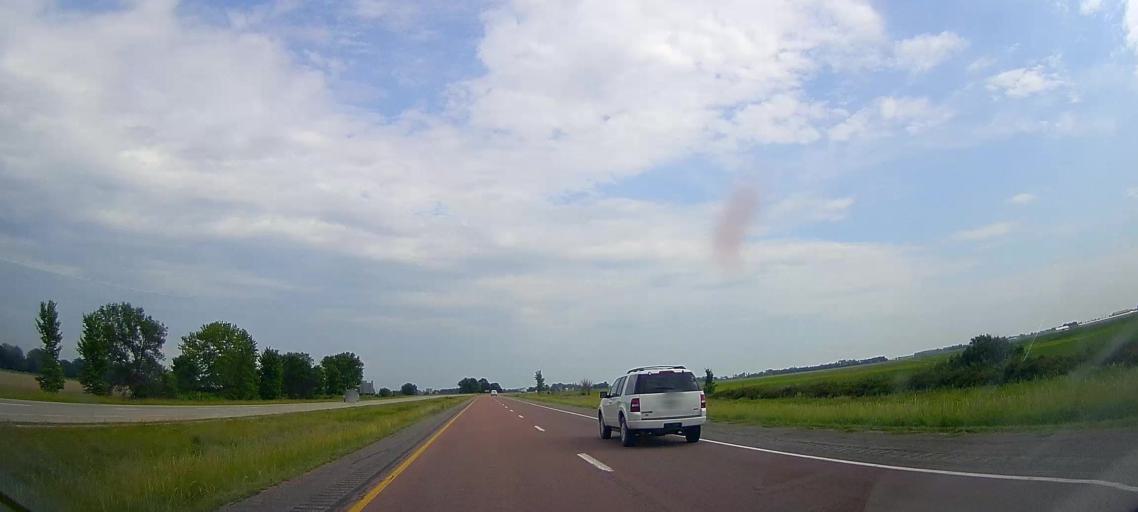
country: US
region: Iowa
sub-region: Monona County
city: Onawa
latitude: 42.0121
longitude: -96.1206
